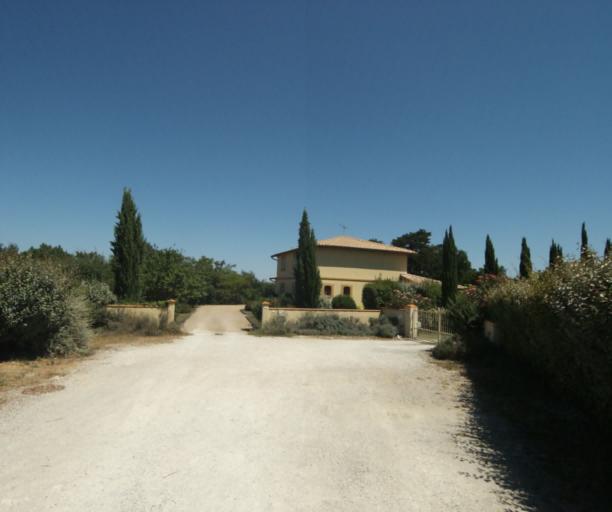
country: FR
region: Midi-Pyrenees
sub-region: Departement de la Haute-Garonne
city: Saint-Felix-Lauragais
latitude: 43.4811
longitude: 1.9210
